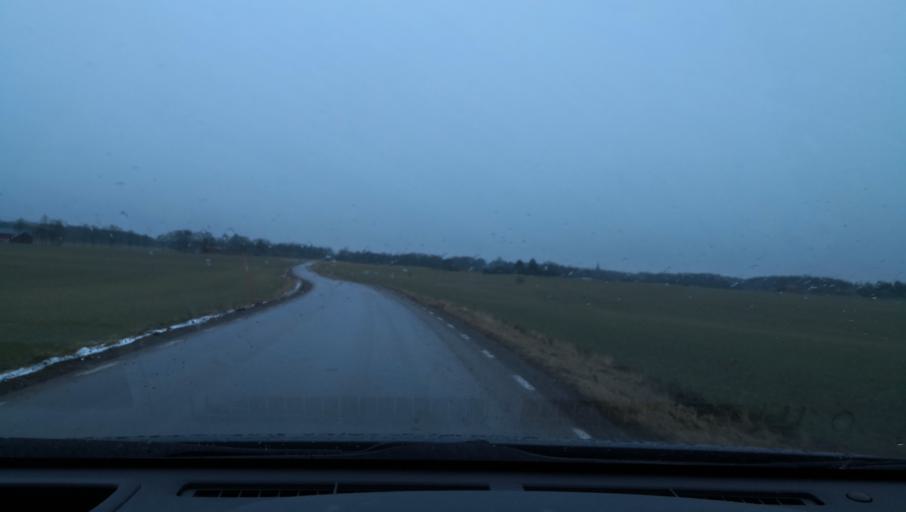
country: SE
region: Soedermanland
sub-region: Eskilstuna Kommun
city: Arla
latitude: 59.4300
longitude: 16.7100
